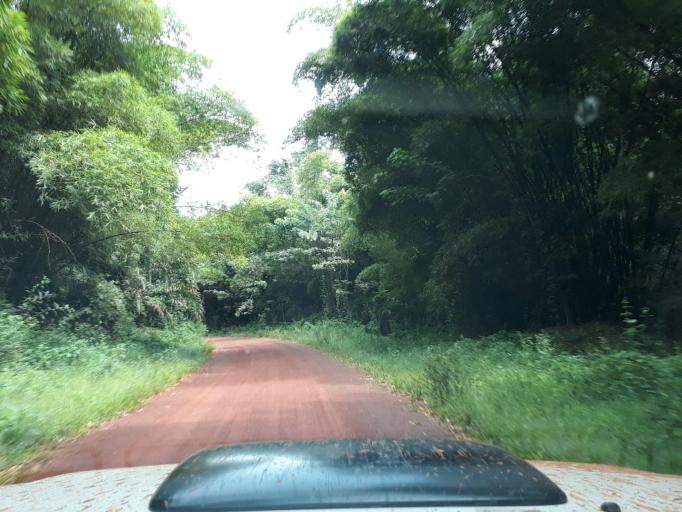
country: CD
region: Eastern Province
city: Buta
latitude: 2.2907
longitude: 25.0528
